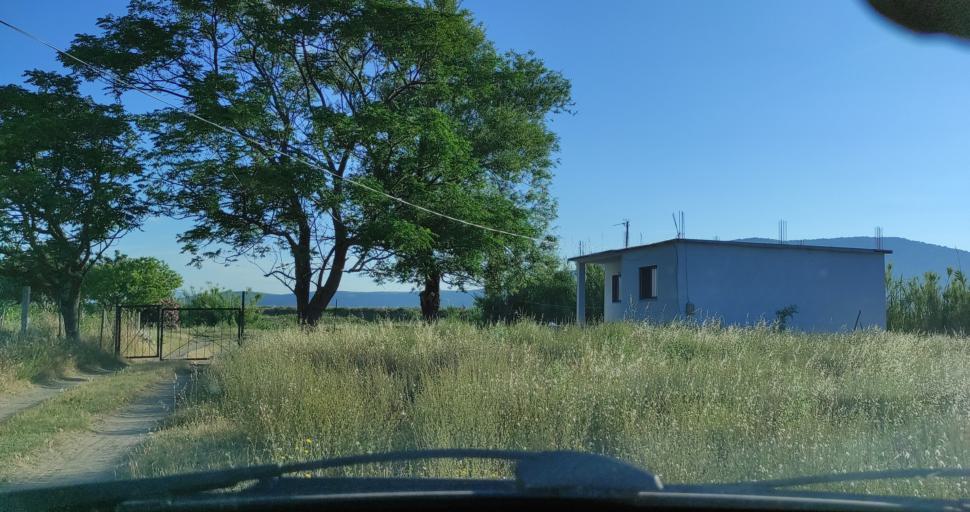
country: AL
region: Shkoder
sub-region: Rrethi i Shkodres
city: Velipoje
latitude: 41.8698
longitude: 19.4355
